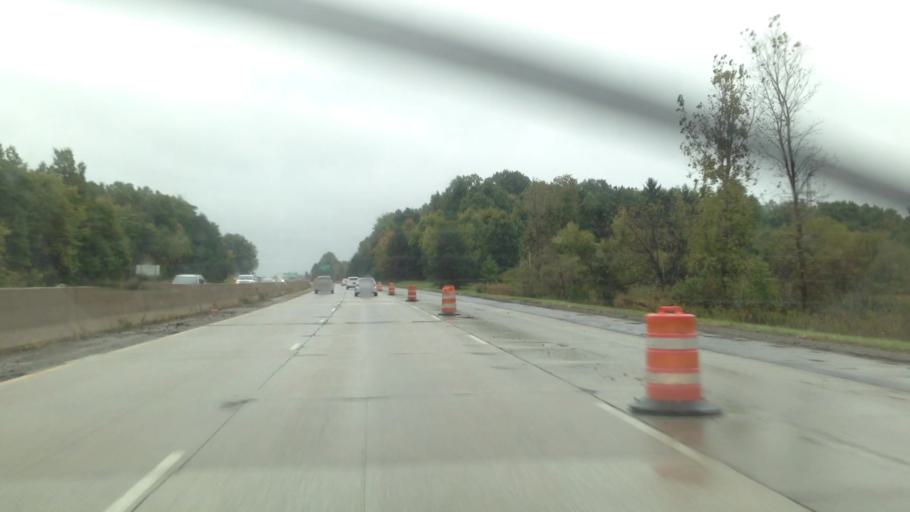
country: US
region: Ohio
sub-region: Summit County
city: Hudson
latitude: 41.2146
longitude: -81.4884
